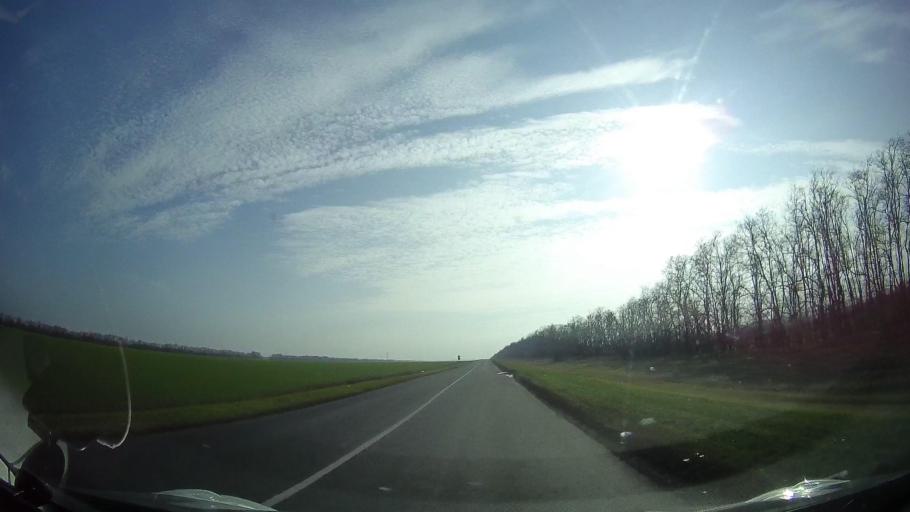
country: RU
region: Rostov
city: Mechetinskaya
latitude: 46.9006
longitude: 40.5418
